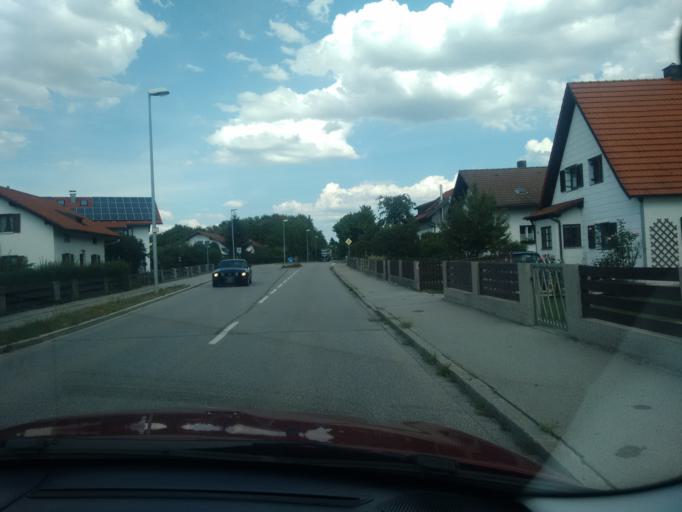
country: DE
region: Bavaria
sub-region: Upper Bavaria
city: Trostberg an der Alz
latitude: 48.0322
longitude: 12.5674
